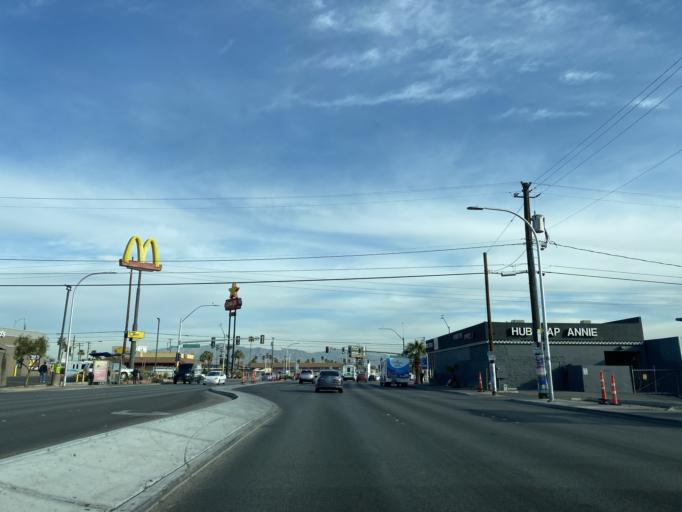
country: US
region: Nevada
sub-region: Clark County
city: Las Vegas
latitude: 36.1579
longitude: -115.1188
